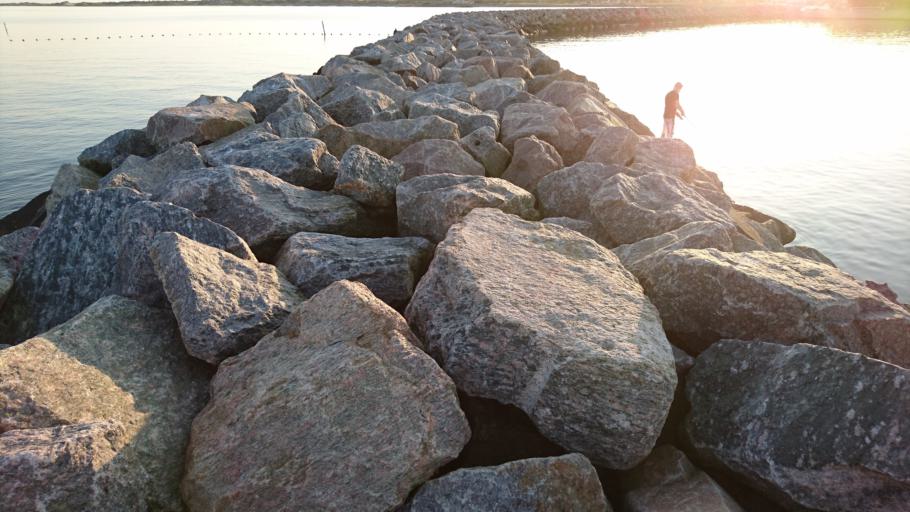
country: DK
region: North Denmark
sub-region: Frederikshavn Kommune
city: Skagen
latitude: 57.7115
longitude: 10.5869
